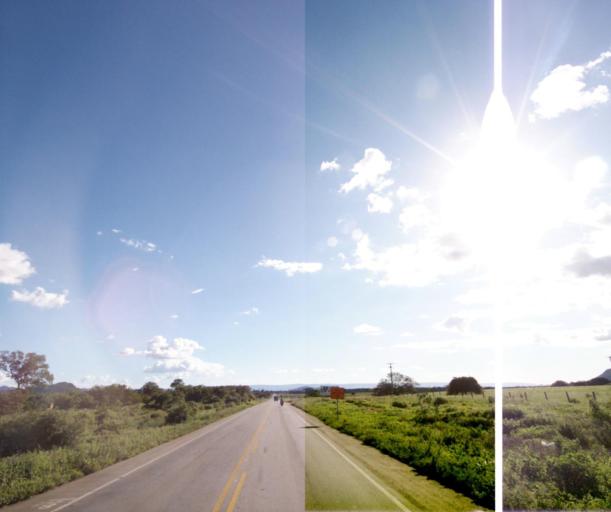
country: BR
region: Bahia
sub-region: Guanambi
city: Guanambi
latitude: -14.1709
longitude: -42.7256
